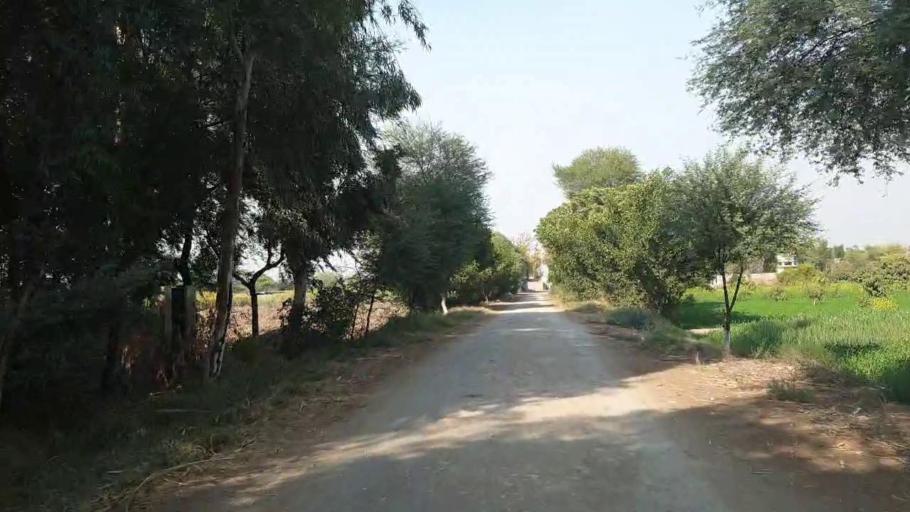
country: PK
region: Sindh
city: Mirwah Gorchani
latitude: 25.3040
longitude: 68.9514
